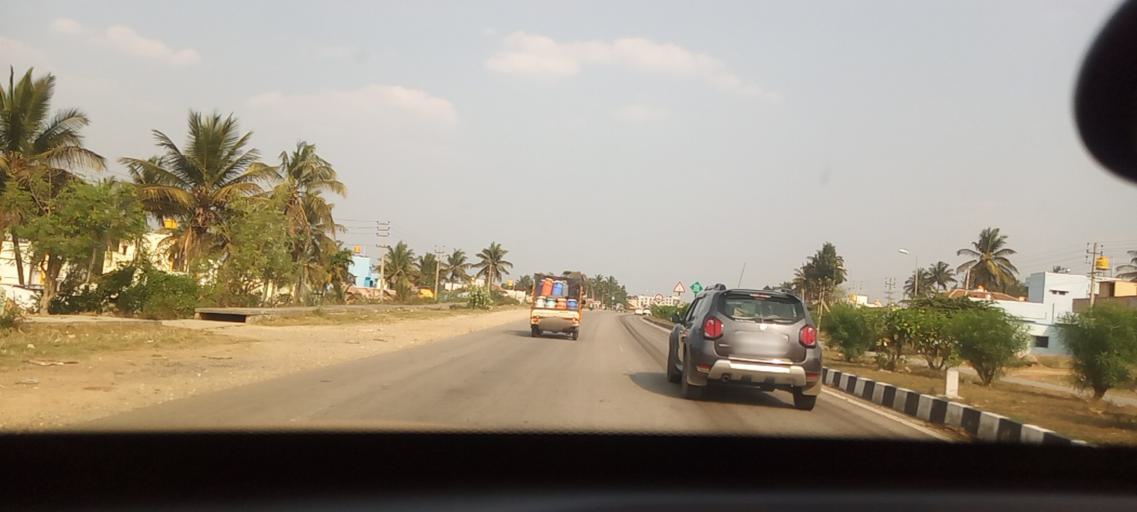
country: IN
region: Karnataka
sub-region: Hassan
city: Hassan
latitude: 12.9961
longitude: 76.1532
